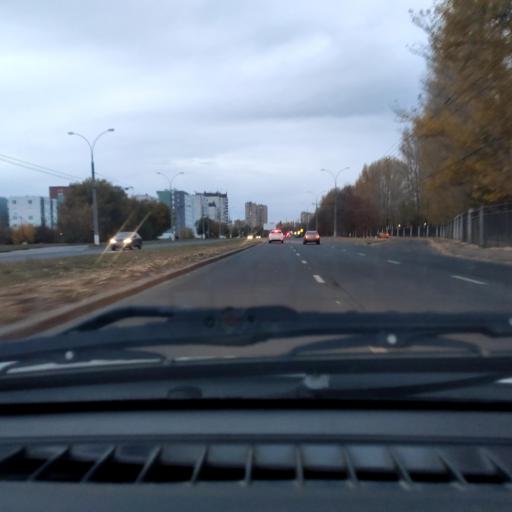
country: RU
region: Samara
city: Tol'yatti
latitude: 53.4996
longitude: 49.2989
